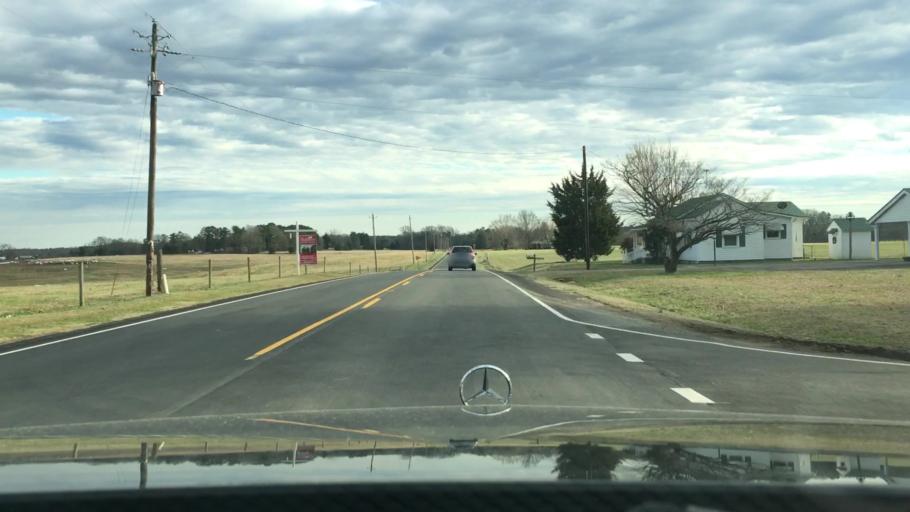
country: US
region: North Carolina
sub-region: Caswell County
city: Yanceyville
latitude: 36.3727
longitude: -79.2589
